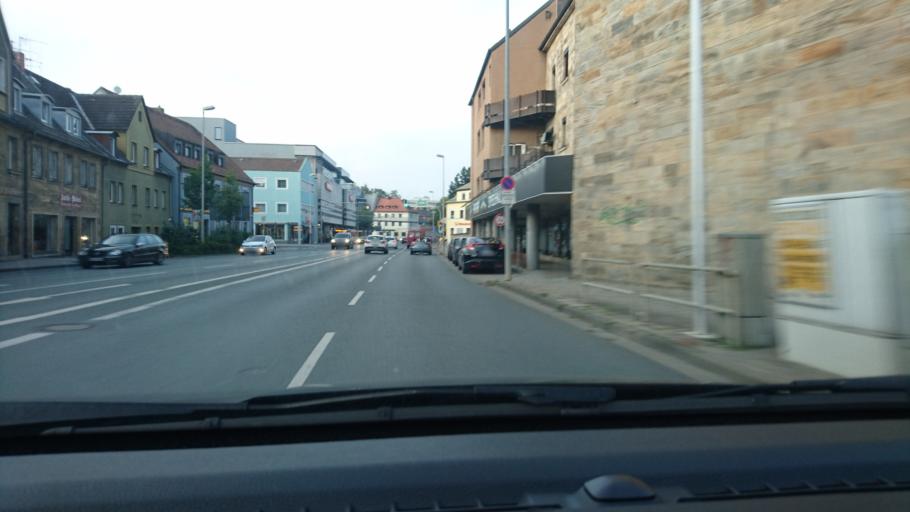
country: DE
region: Bavaria
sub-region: Upper Franconia
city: Bayreuth
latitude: 49.9441
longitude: 11.5702
